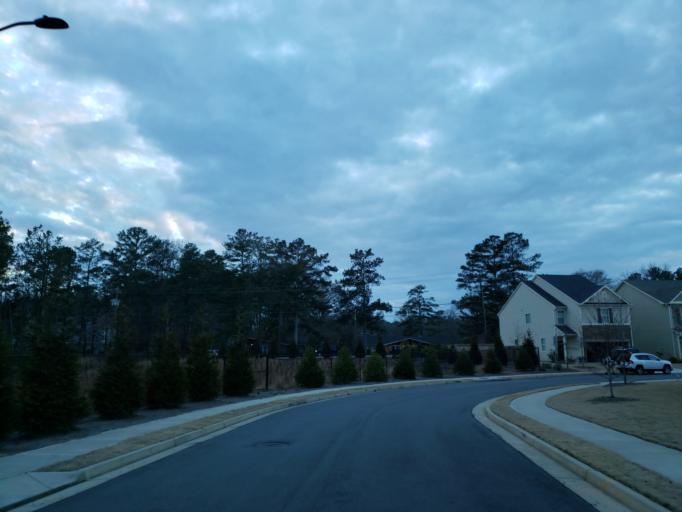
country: US
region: Georgia
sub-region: Cobb County
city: Mableton
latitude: 33.8537
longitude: -84.5875
